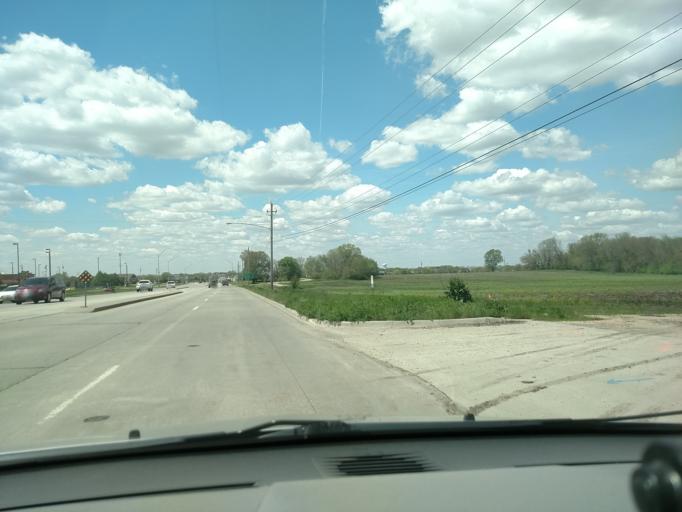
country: US
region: Iowa
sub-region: Polk County
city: Ankeny
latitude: 41.7029
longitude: -93.5955
